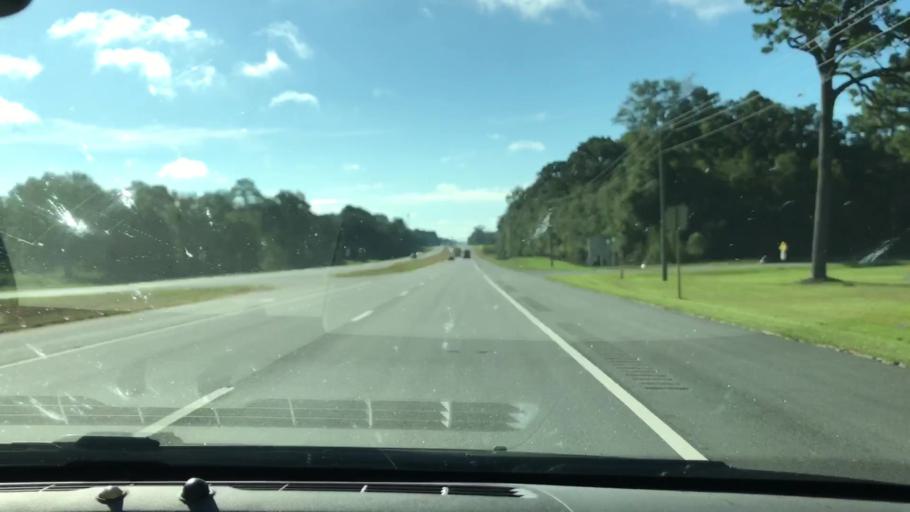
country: US
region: Georgia
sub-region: Lee County
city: Leesburg
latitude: 31.6691
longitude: -84.2864
